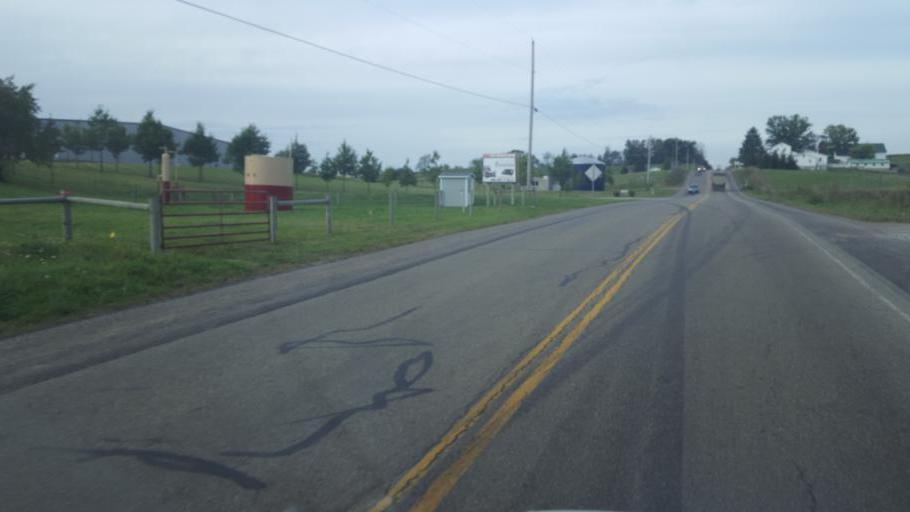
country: US
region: Ohio
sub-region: Holmes County
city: Millersburg
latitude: 40.5805
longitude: -81.7811
